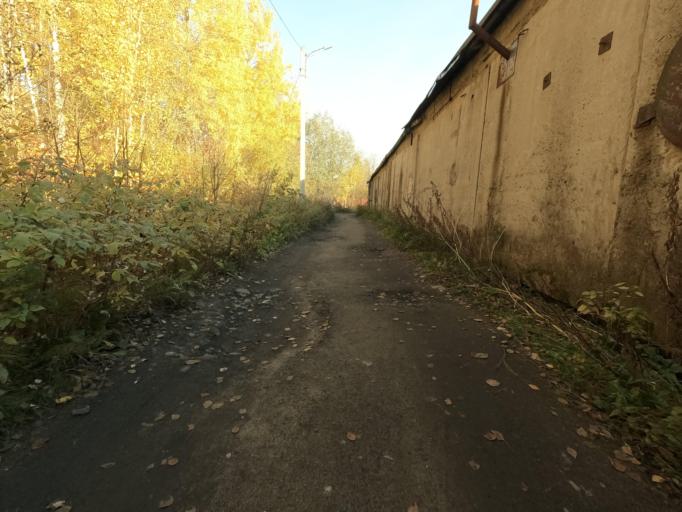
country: RU
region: Leningrad
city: Mga
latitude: 59.7522
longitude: 31.0689
